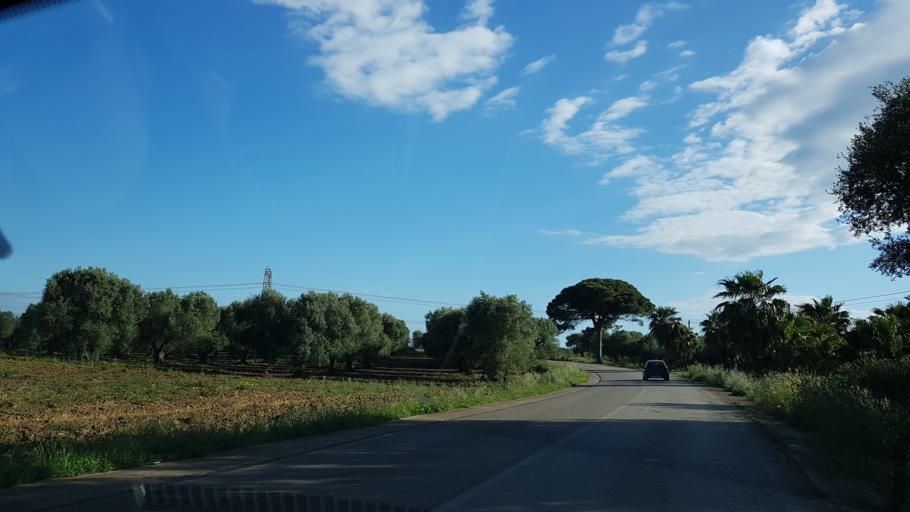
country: IT
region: Apulia
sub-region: Provincia di Brindisi
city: Mesagne
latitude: 40.5854
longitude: 17.8137
